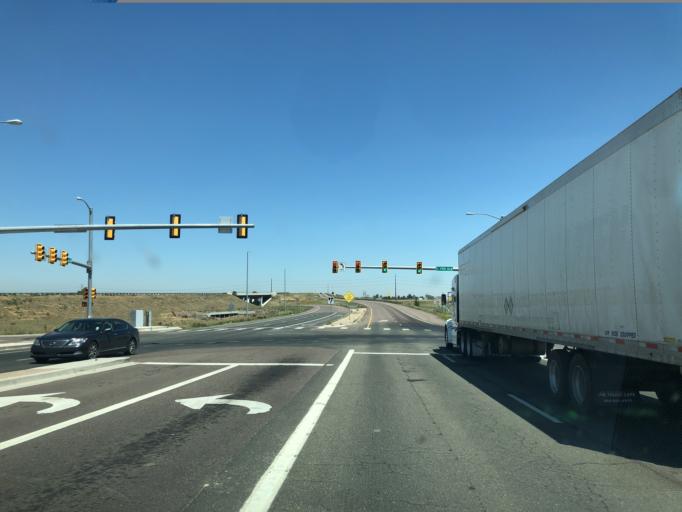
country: US
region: Colorado
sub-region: Adams County
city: Aurora
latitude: 39.7422
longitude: -104.7159
